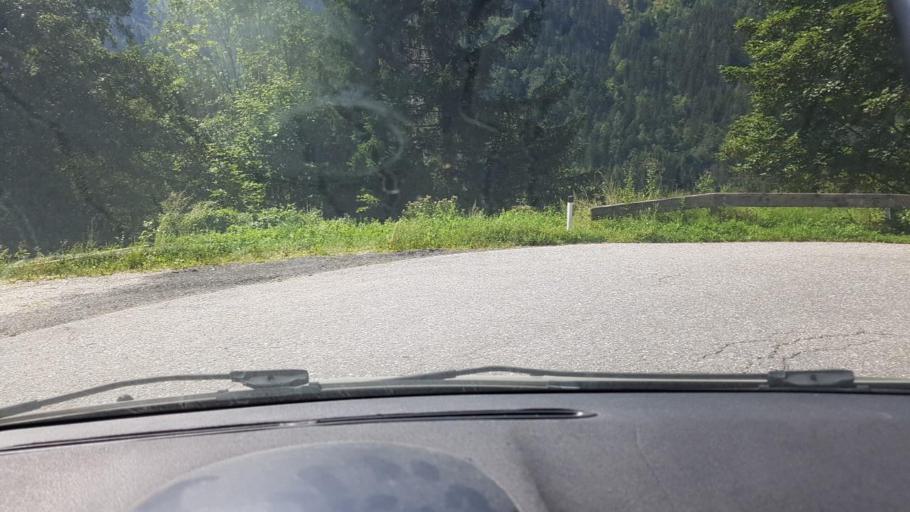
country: SI
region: Jezersko
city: Zgornje Jezersko
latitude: 46.4192
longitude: 14.5573
